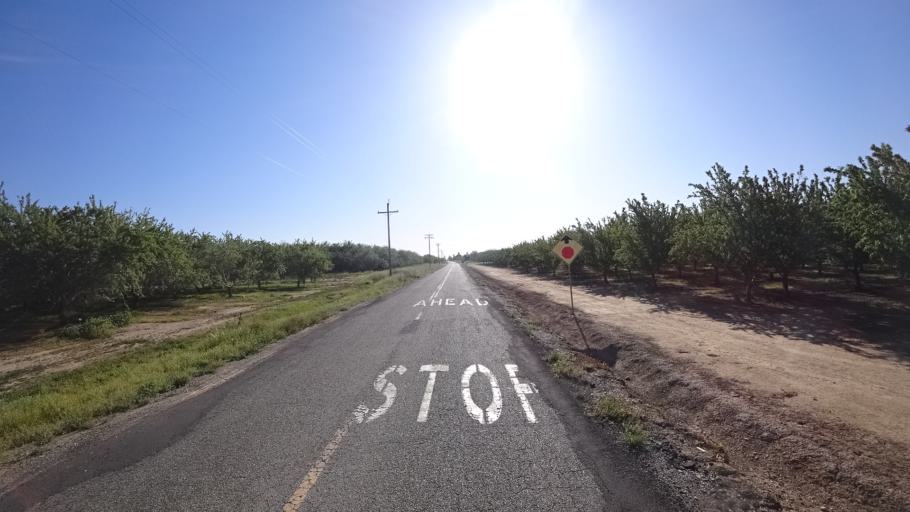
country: US
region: California
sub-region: Glenn County
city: Hamilton City
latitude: 39.6959
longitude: -122.1054
